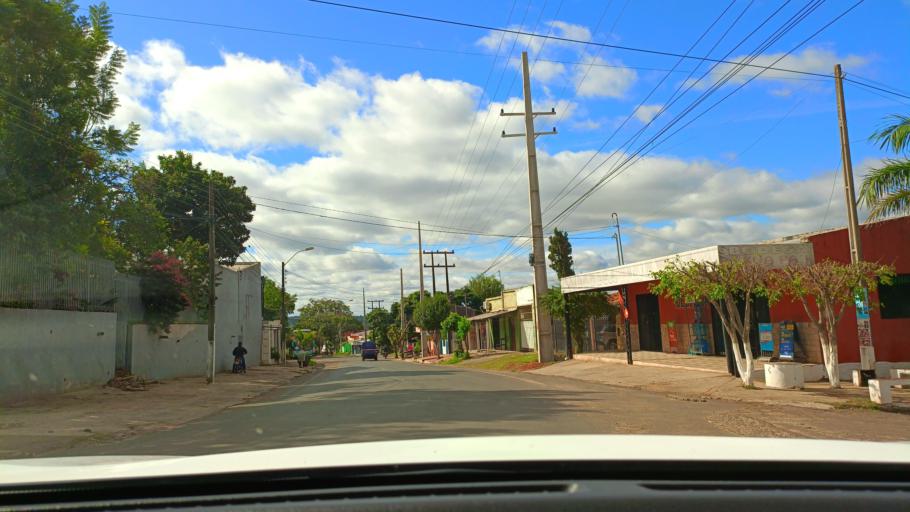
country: PY
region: San Pedro
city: Guayaybi
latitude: -24.6680
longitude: -56.4404
